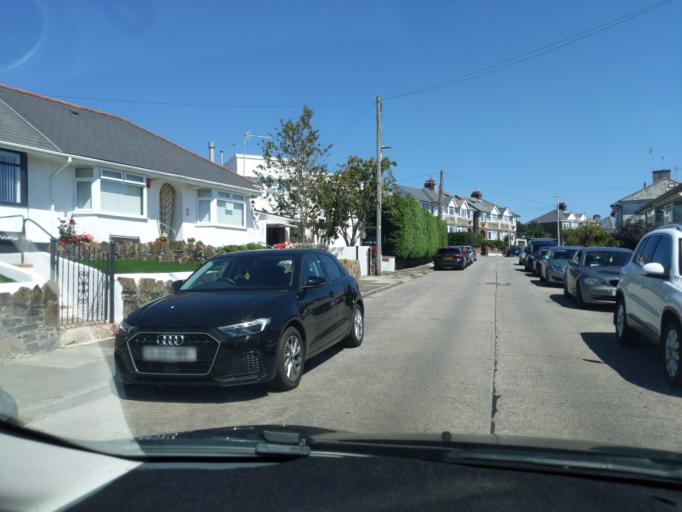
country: GB
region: England
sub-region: Plymouth
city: Plymouth
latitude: 50.3898
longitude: -4.1576
